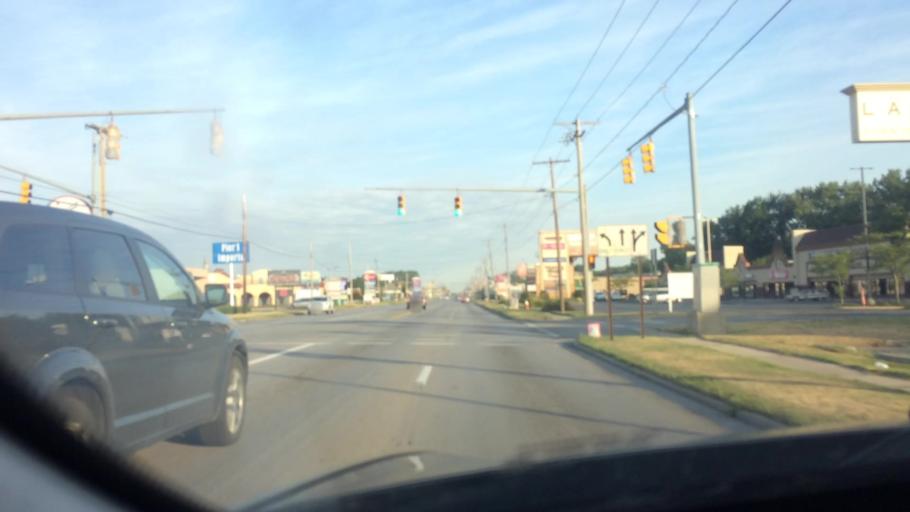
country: US
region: Ohio
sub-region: Lucas County
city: Ottawa Hills
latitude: 41.7006
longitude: -83.6489
